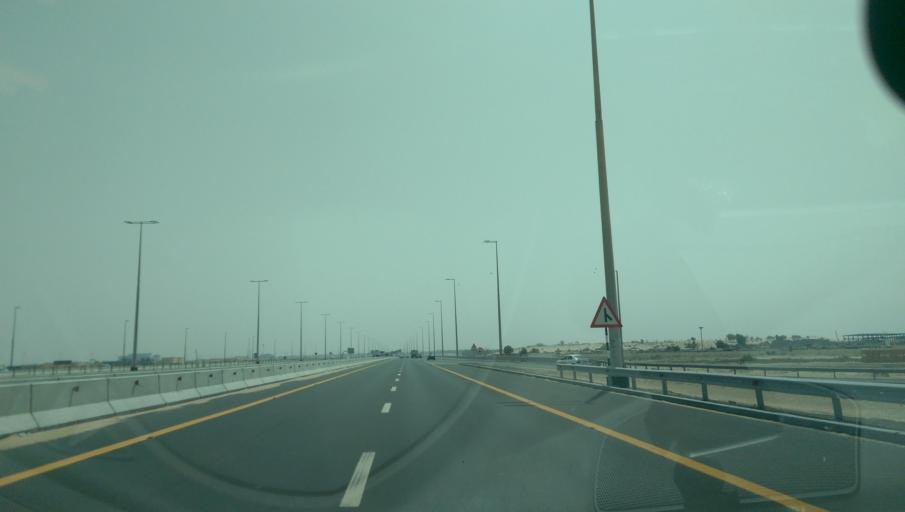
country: AE
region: Abu Dhabi
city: Abu Dhabi
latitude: 24.2963
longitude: 54.5787
